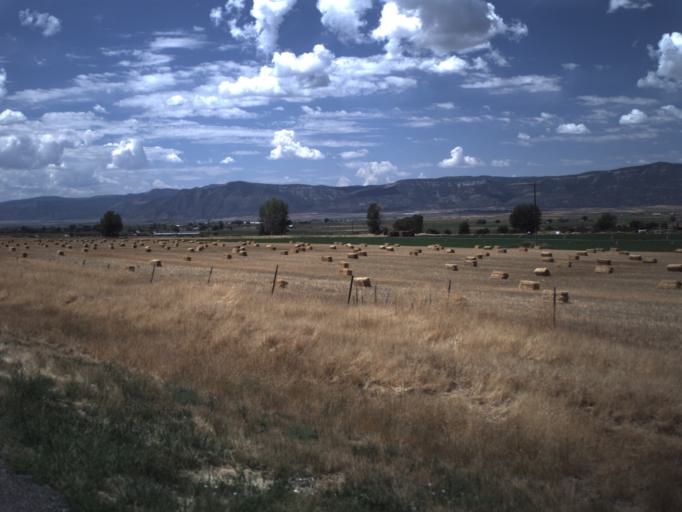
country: US
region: Utah
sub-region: Sanpete County
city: Mount Pleasant
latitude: 39.5143
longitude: -111.4783
